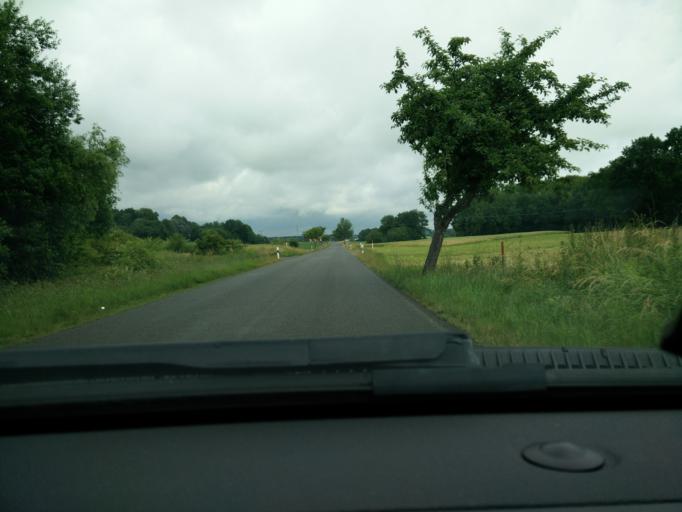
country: DE
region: Saxony
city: Geithain
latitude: 51.0780
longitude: 12.6902
